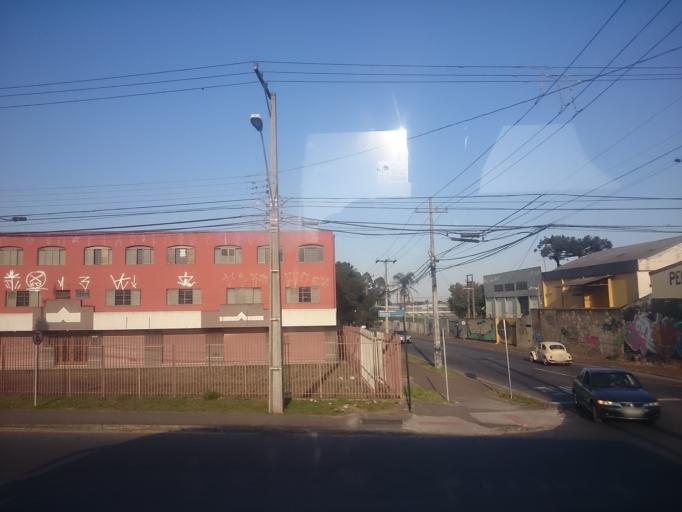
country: BR
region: Parana
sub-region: Sao Jose Dos Pinhais
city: Sao Jose dos Pinhais
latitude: -25.5209
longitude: -49.2940
